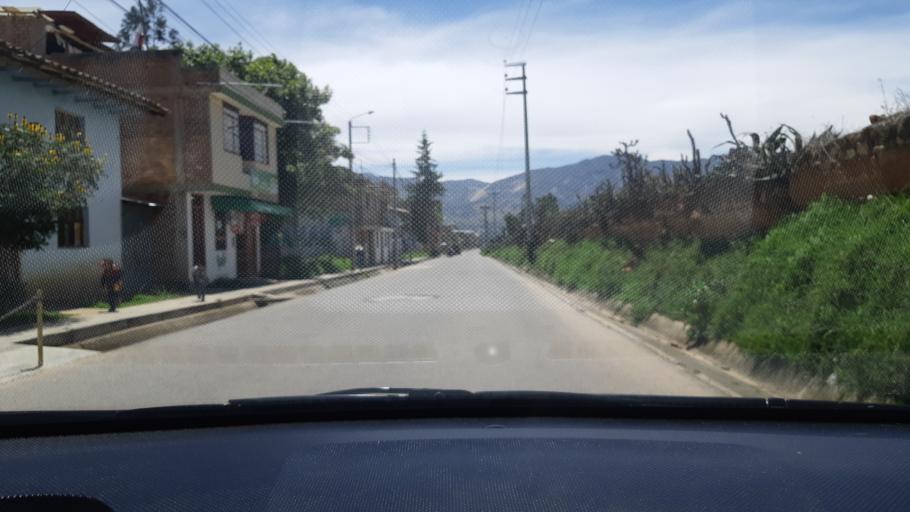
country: PE
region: Cajamarca
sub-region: Provincia de Cajamarca
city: Llacanora
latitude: -7.1700
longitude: -78.4575
